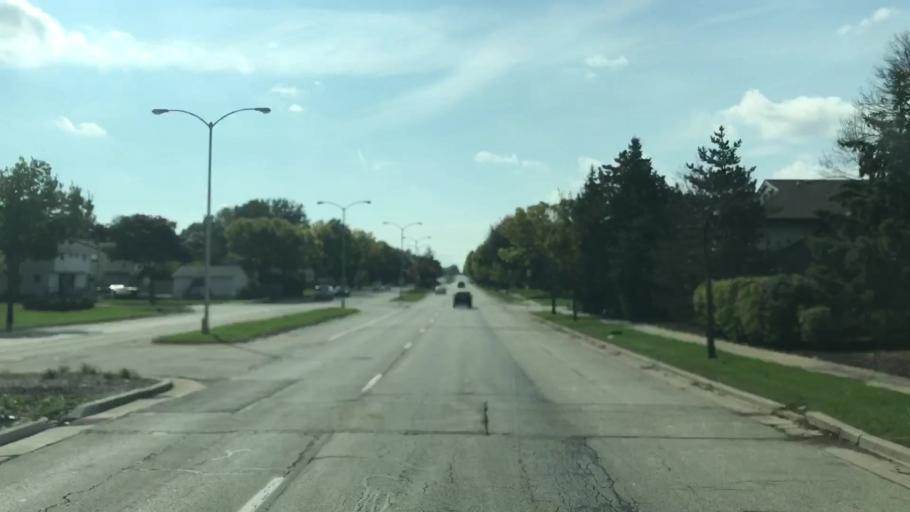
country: US
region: Wisconsin
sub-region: Waukesha County
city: Butler
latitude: 43.1719
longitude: -88.0444
